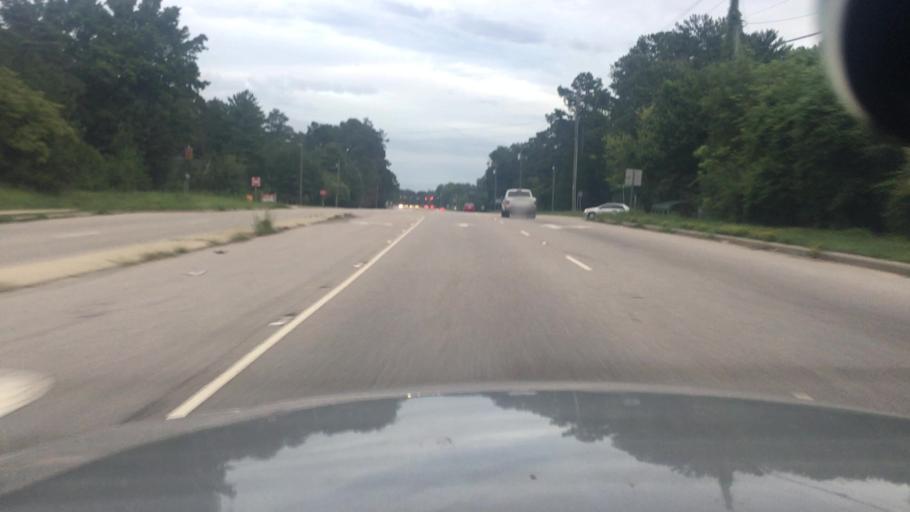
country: US
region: North Carolina
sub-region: Cumberland County
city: Hope Mills
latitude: 34.9990
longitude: -78.9729
